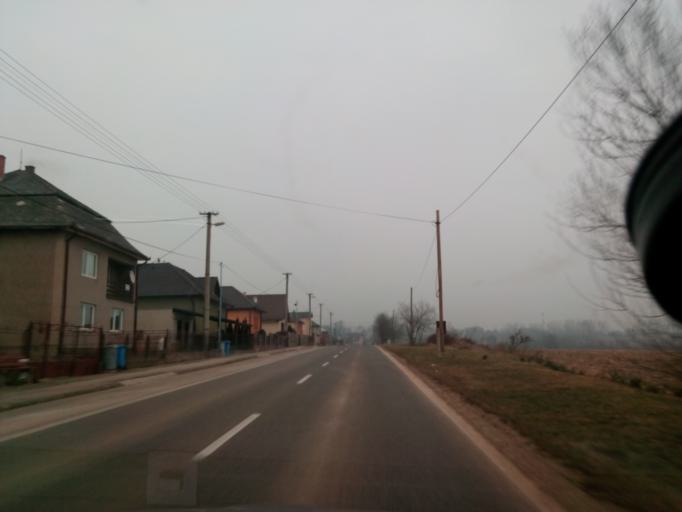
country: SK
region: Kosicky
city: Moldava nad Bodvou
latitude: 48.6771
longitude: 21.0968
